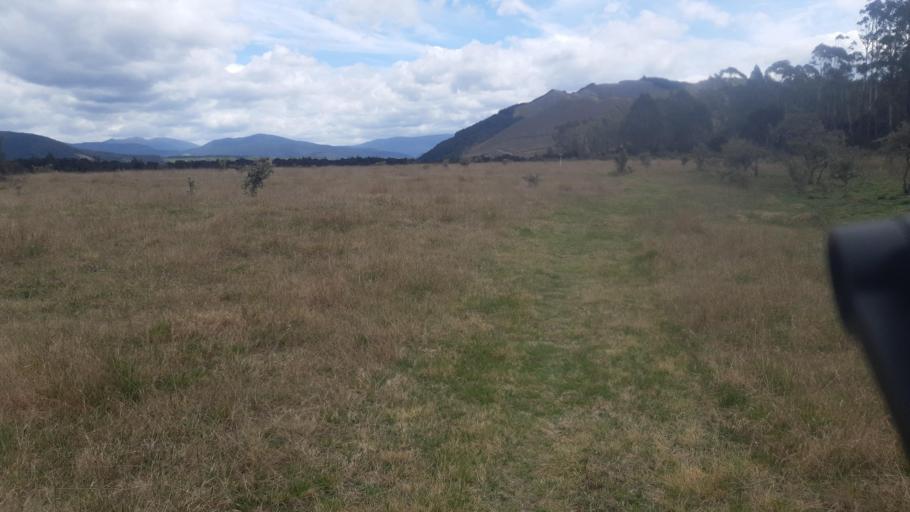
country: NZ
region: Tasman
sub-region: Tasman District
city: Wakefield
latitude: -41.7735
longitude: 172.8035
